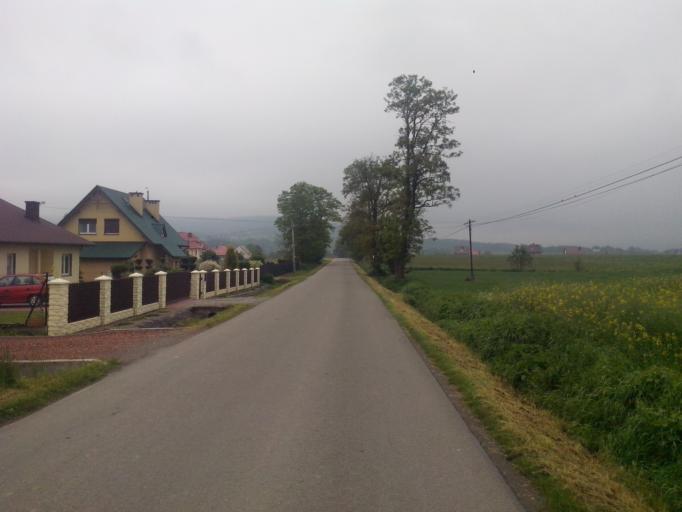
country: PL
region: Subcarpathian Voivodeship
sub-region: Powiat strzyzowski
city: Strzyzow
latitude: 49.8537
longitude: 21.7796
